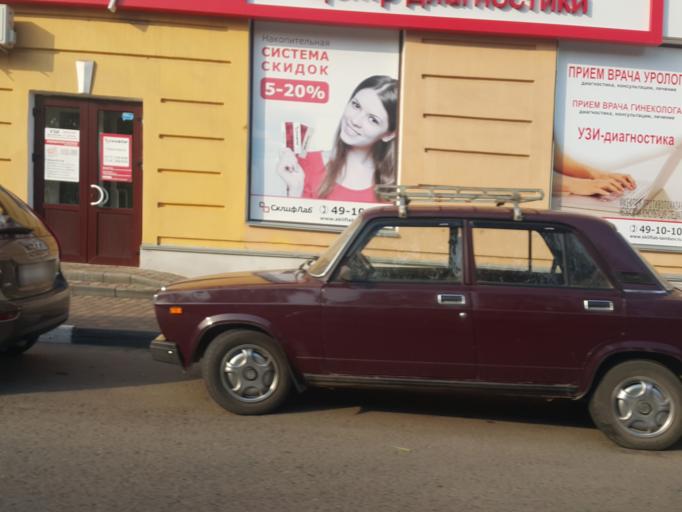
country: RU
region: Tambov
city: Tambov
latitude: 52.7234
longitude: 41.4512
